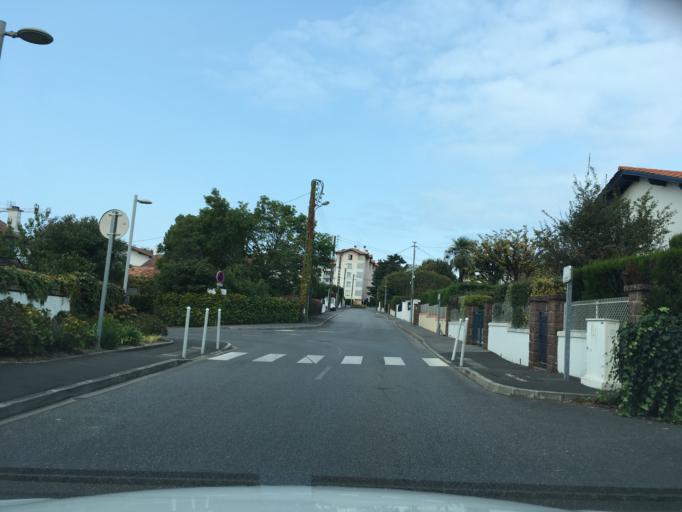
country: FR
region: Aquitaine
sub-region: Departement des Pyrenees-Atlantiques
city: Anglet
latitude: 43.4858
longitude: -1.5053
